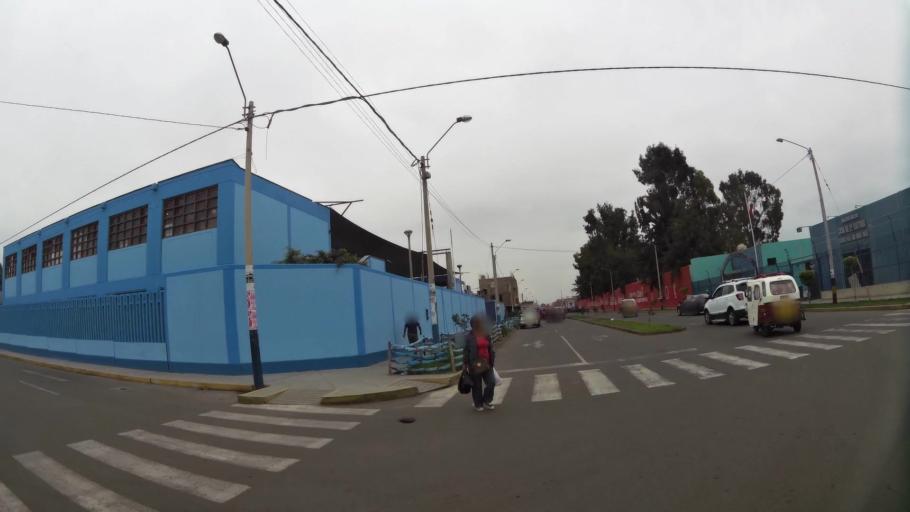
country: PE
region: Ica
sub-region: Provincia de Pisco
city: Pisco
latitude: -13.7112
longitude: -76.2076
